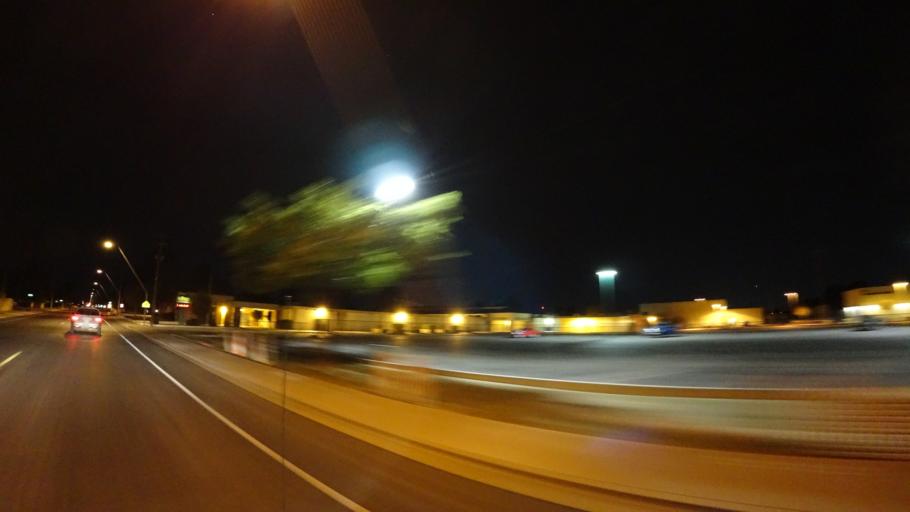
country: US
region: Arizona
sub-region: Maricopa County
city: Mesa
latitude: 33.4322
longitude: -111.8140
